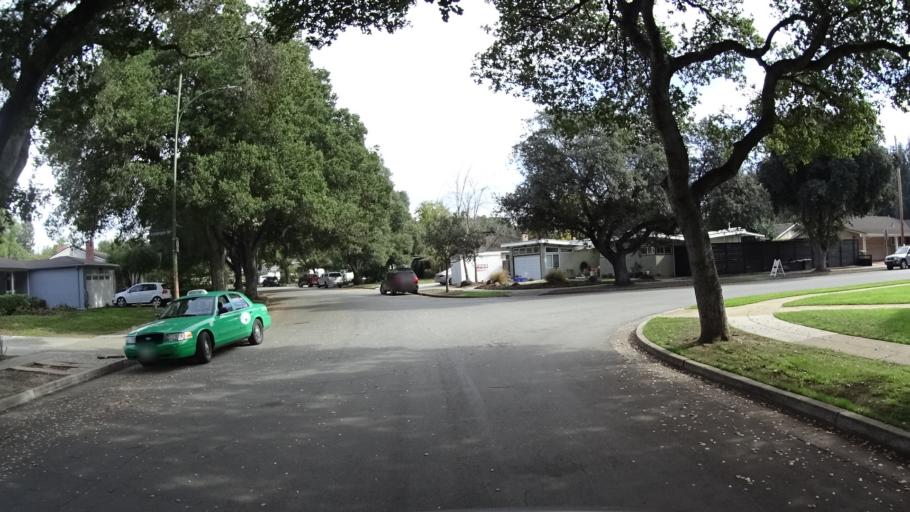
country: US
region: California
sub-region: Santa Clara County
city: Burbank
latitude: 37.3311
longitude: -121.9375
